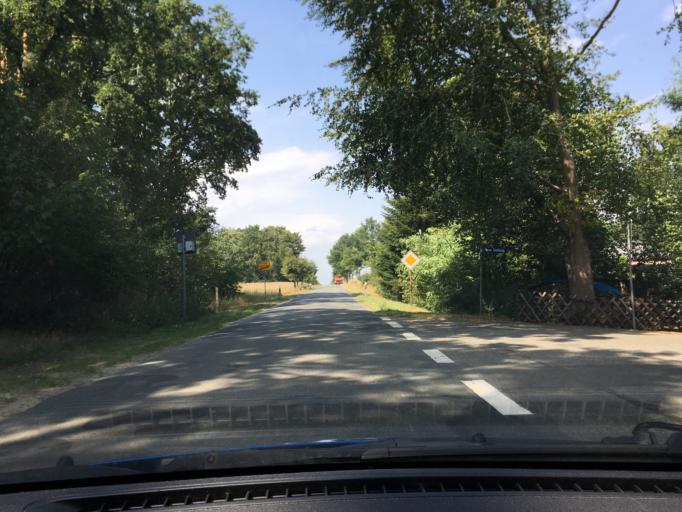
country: DE
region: Lower Saxony
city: Natendorf
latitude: 53.1122
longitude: 10.4485
